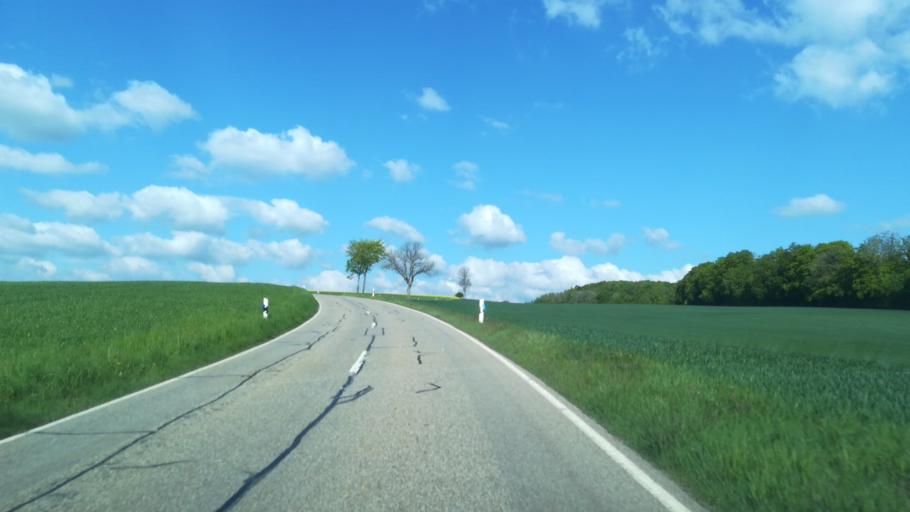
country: DE
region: Baden-Wuerttemberg
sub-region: Freiburg Region
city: Stuhlingen
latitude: 47.7463
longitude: 8.4275
